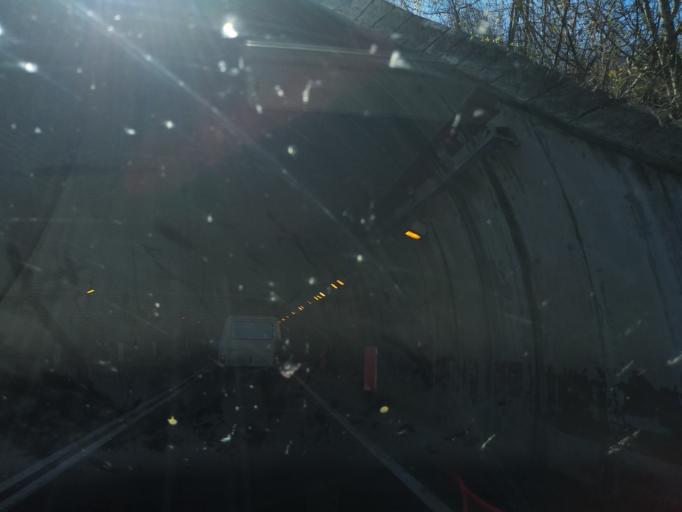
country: IT
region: Emilia-Romagna
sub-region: Provincia di Reggio Emilia
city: Casina
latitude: 44.5193
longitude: 10.4976
